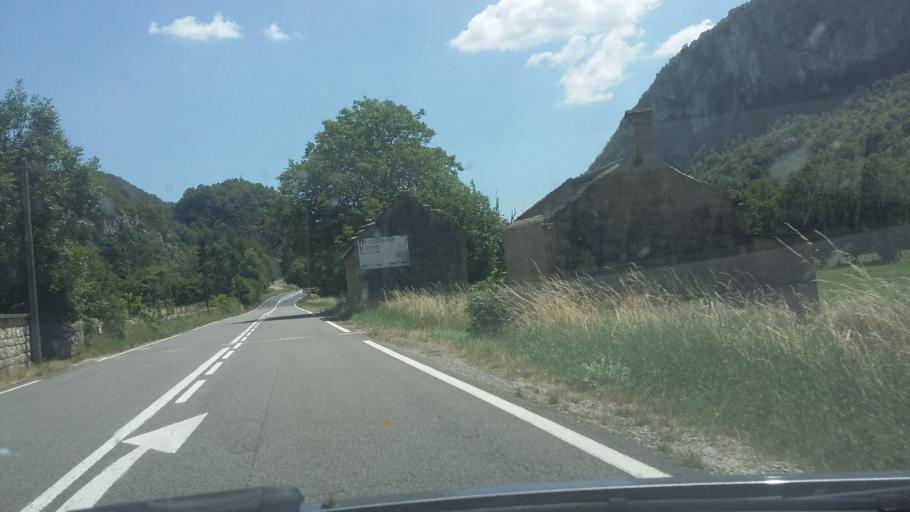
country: FR
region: Rhone-Alpes
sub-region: Departement de l'Ain
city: Virieu-le-Grand
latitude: 45.8361
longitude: 5.5873
